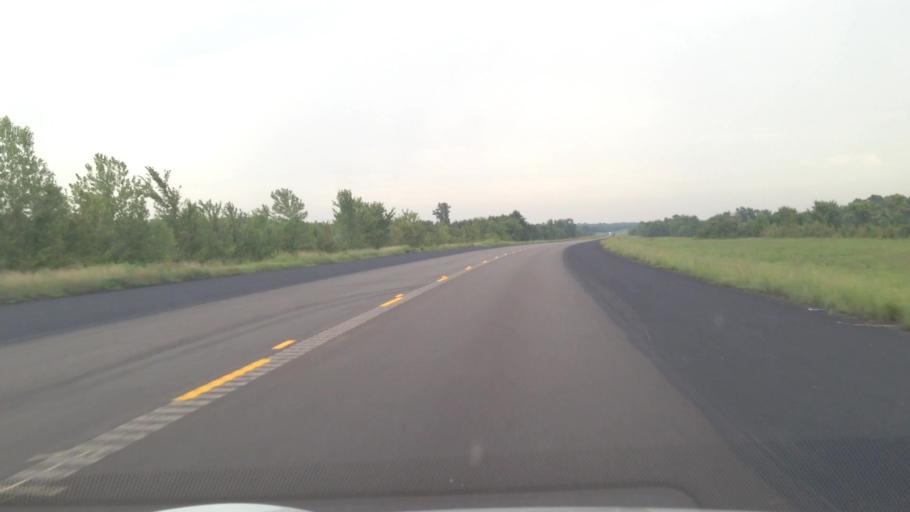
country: US
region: Kansas
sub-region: Cherokee County
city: Baxter Springs
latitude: 37.0449
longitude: -94.7123
